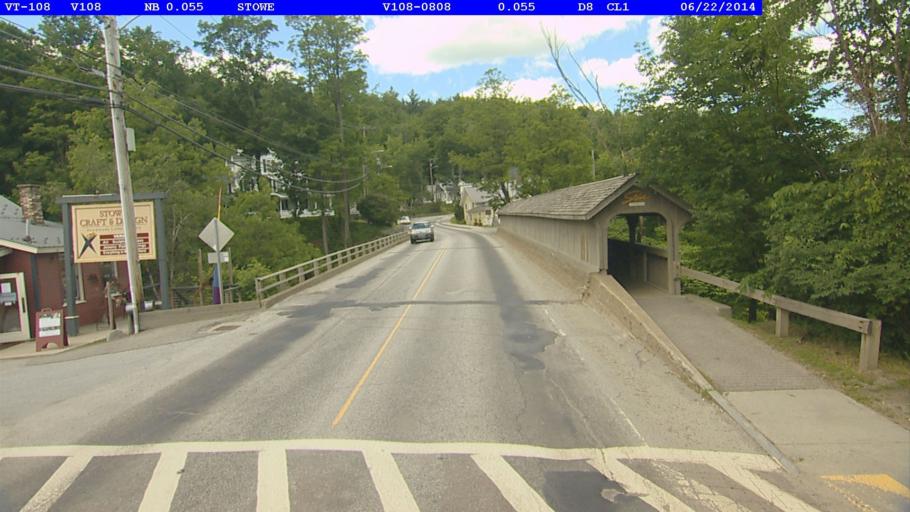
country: US
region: Vermont
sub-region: Lamoille County
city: Morristown
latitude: 44.4662
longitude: -72.6879
